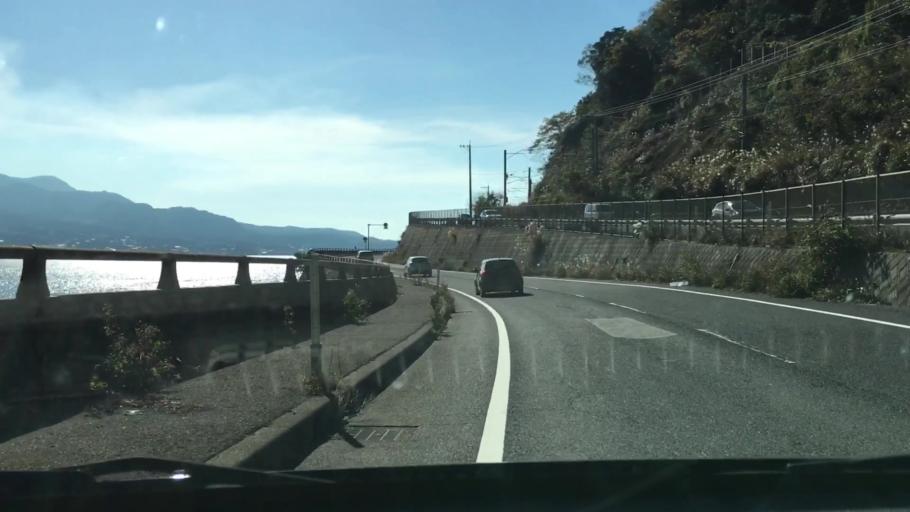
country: JP
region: Kagoshima
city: Kagoshima-shi
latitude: 31.6400
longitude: 130.6024
